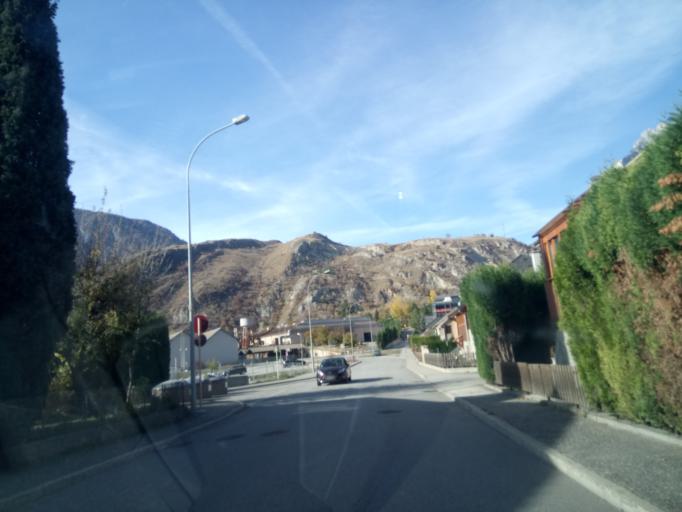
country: FR
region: Rhone-Alpes
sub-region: Departement de la Savoie
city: Saint-Michel-de-Maurienne
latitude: 45.2209
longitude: 6.4670
